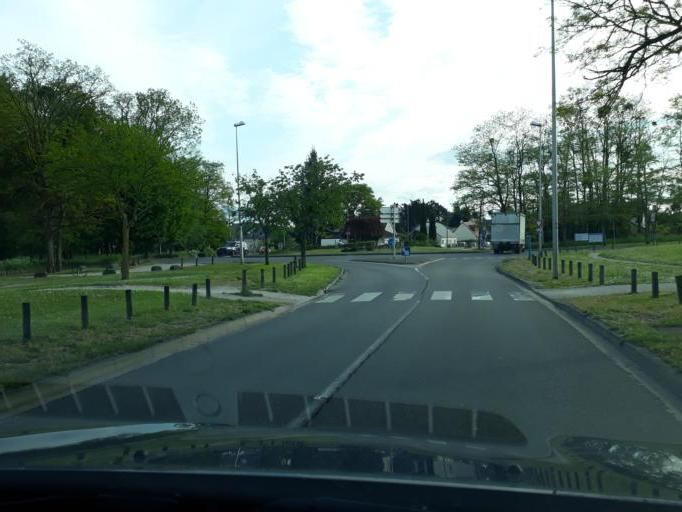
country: FR
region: Centre
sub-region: Departement du Loiret
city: Ingre
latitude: 47.9195
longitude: 1.8349
